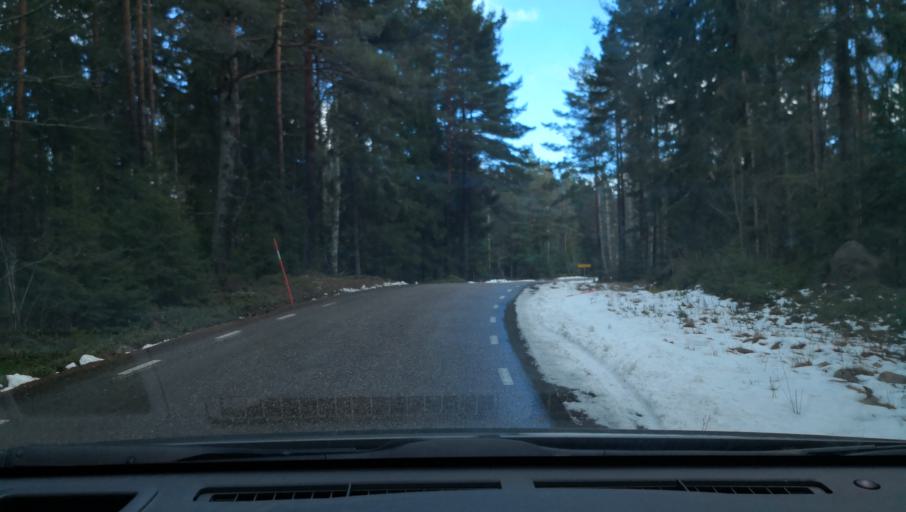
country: SE
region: Vaestmanland
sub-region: Arboga Kommun
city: Arboga
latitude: 59.3341
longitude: 15.7245
